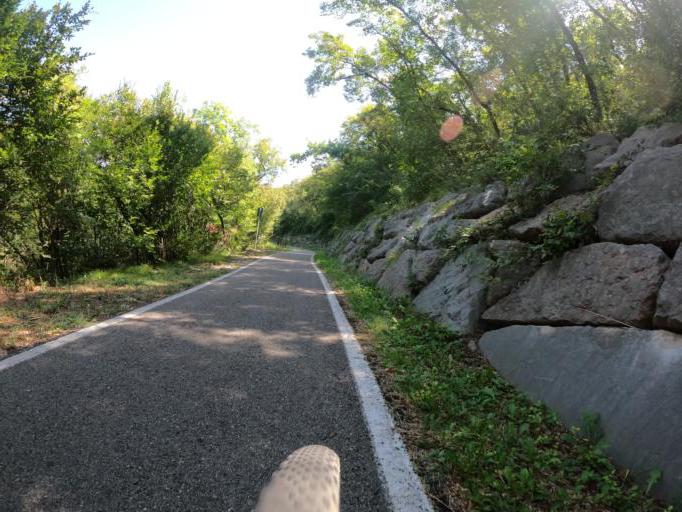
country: IT
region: Veneto
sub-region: Provincia di Verona
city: Rivoli Veronese
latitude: 45.5593
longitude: 10.8237
